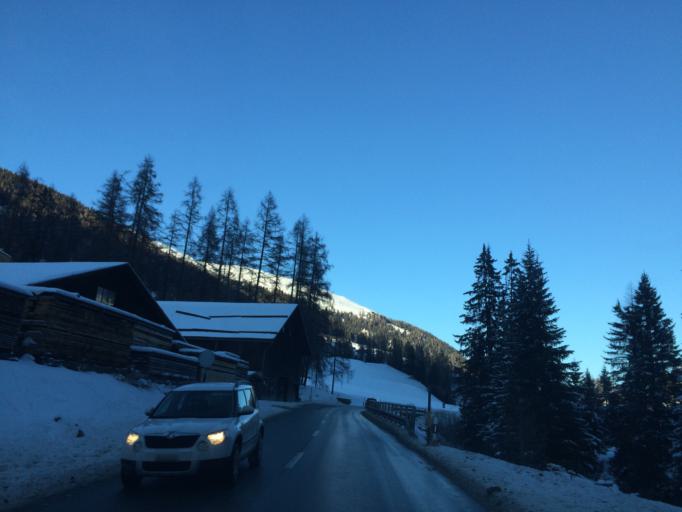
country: CH
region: Grisons
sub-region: Praettigau/Davos District
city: Davos
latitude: 46.7515
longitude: 9.7841
